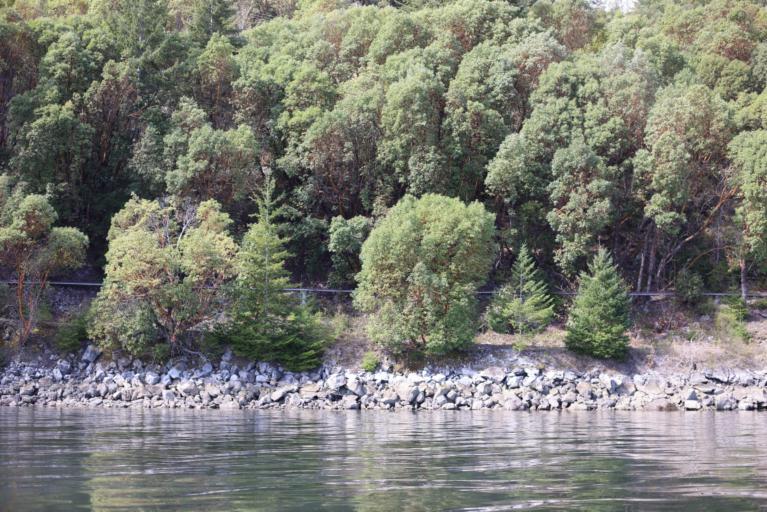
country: CA
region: British Columbia
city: North Saanich
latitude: 48.5881
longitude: -123.5206
